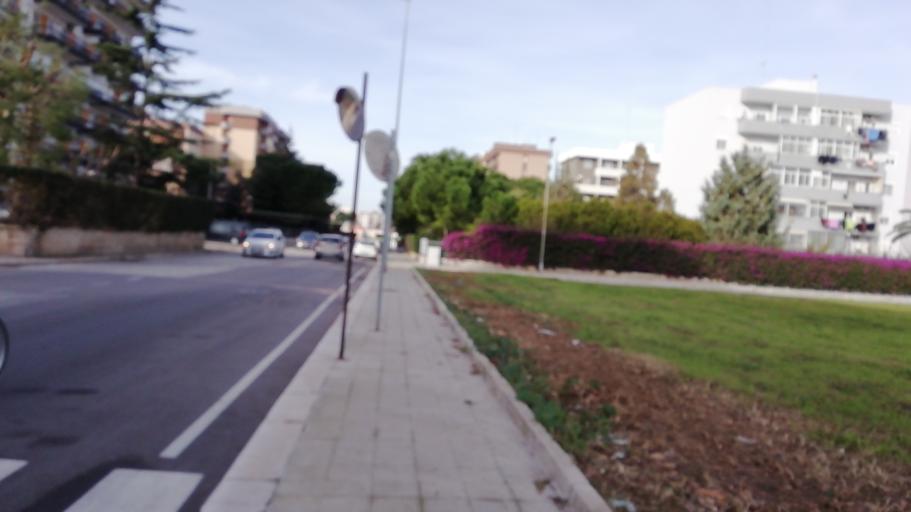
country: IT
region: Apulia
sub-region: Provincia di Bari
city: Triggiano
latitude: 41.1030
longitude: 16.9148
